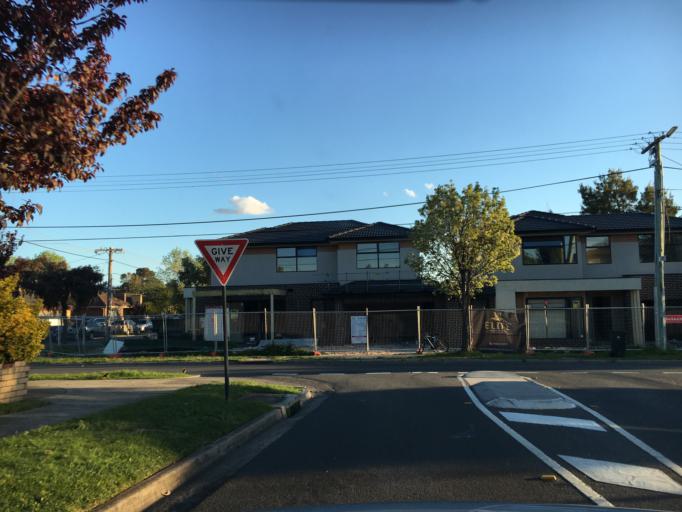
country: AU
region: Victoria
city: Clayton
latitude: -37.9069
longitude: 145.1106
